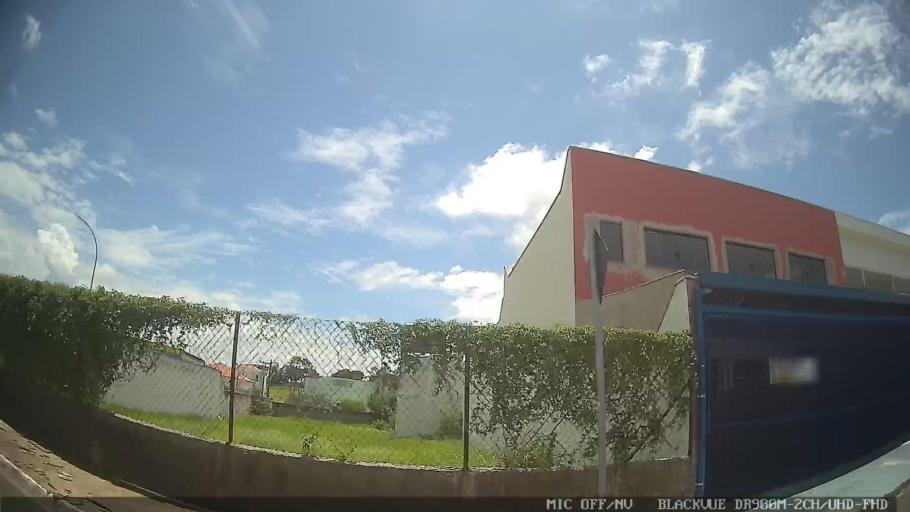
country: BR
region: Sao Paulo
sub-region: Laranjal Paulista
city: Laranjal Paulista
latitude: -23.0426
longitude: -47.8392
